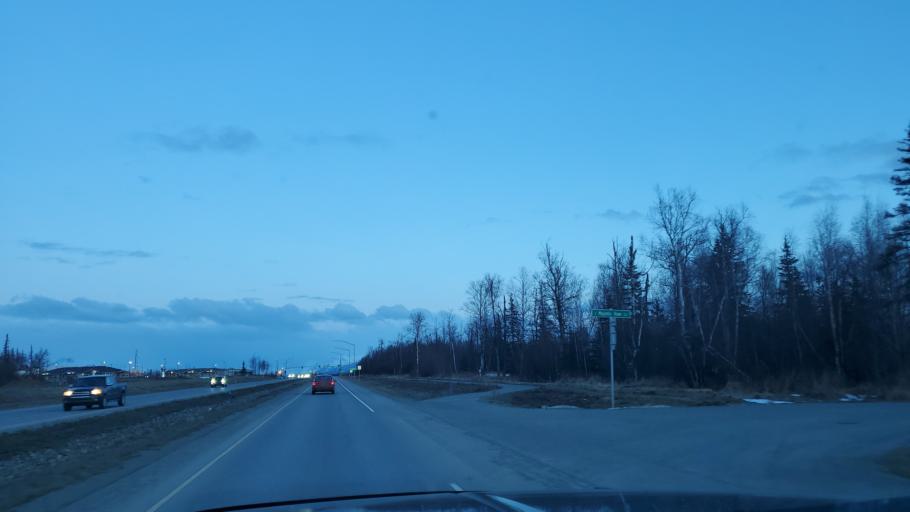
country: US
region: Alaska
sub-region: Matanuska-Susitna Borough
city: Wasilla
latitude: 61.5721
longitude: -149.4282
